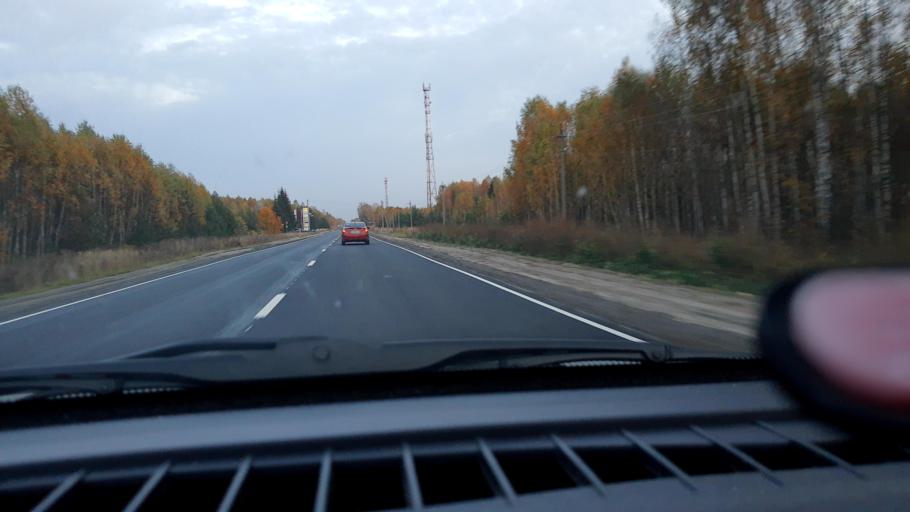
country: RU
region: Nizjnij Novgorod
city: Novaya Balakhna
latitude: 56.6018
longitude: 43.6297
